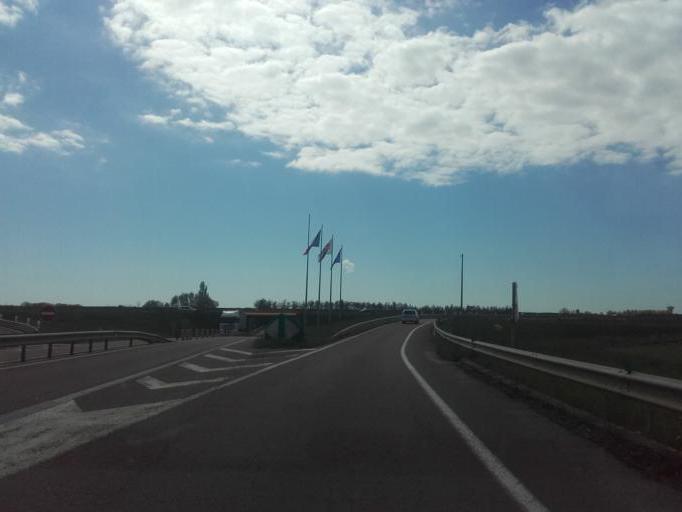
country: FR
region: Bourgogne
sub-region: Departement de la Cote-d'Or
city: Nuits-Saint-Georges
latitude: 47.1298
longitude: 4.9692
